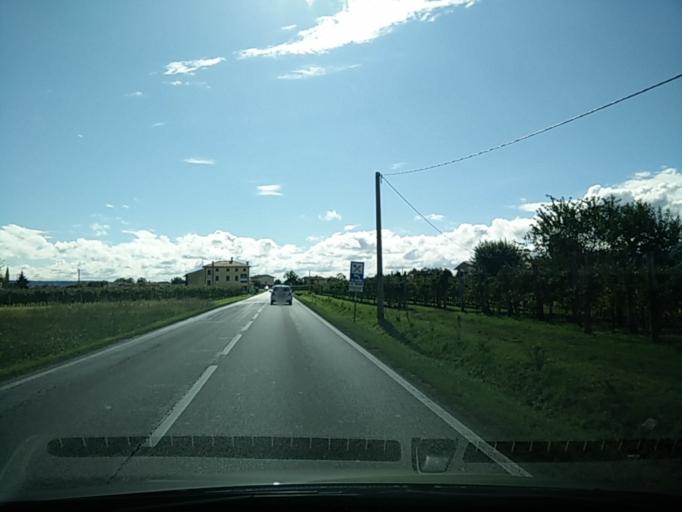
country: IT
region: Veneto
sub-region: Provincia di Treviso
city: Bigolino
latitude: 45.8762
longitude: 12.0033
